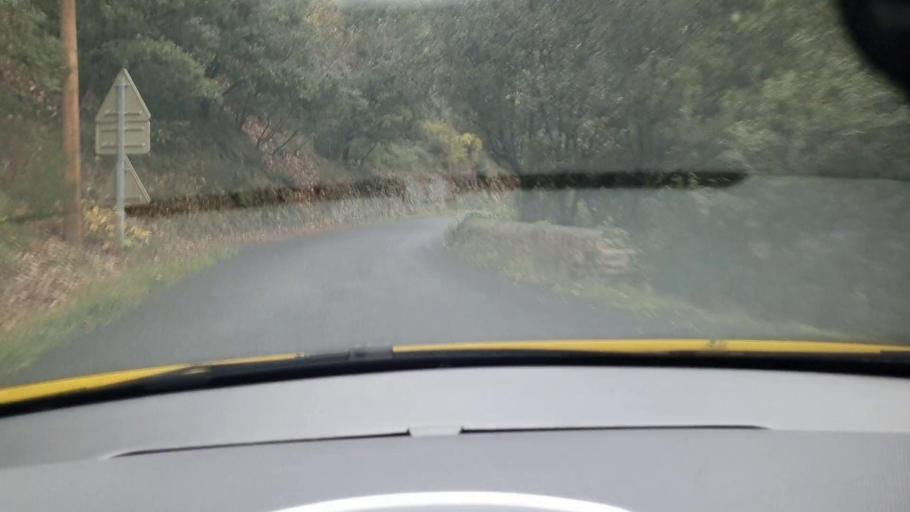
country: FR
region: Languedoc-Roussillon
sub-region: Departement du Gard
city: Sumene
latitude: 44.0252
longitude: 3.7325
